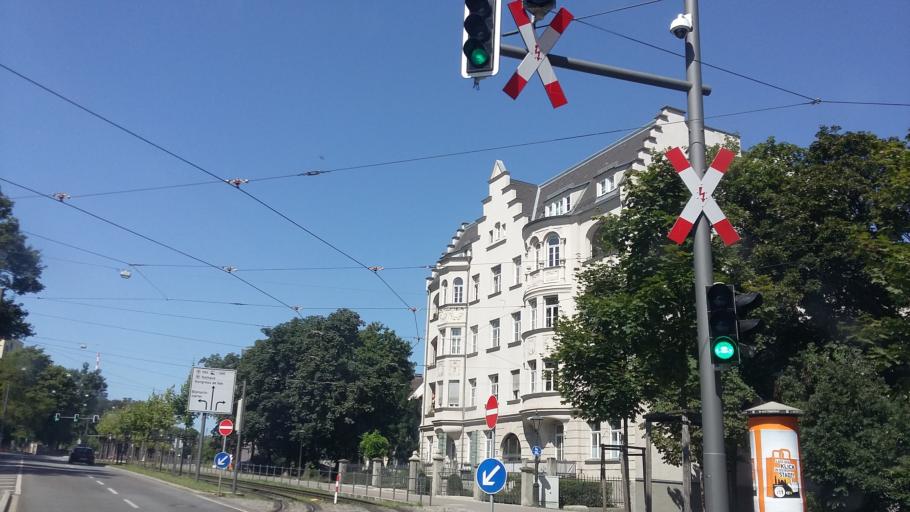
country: DE
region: Bavaria
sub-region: Swabia
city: Augsburg
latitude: 48.3596
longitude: 10.9020
